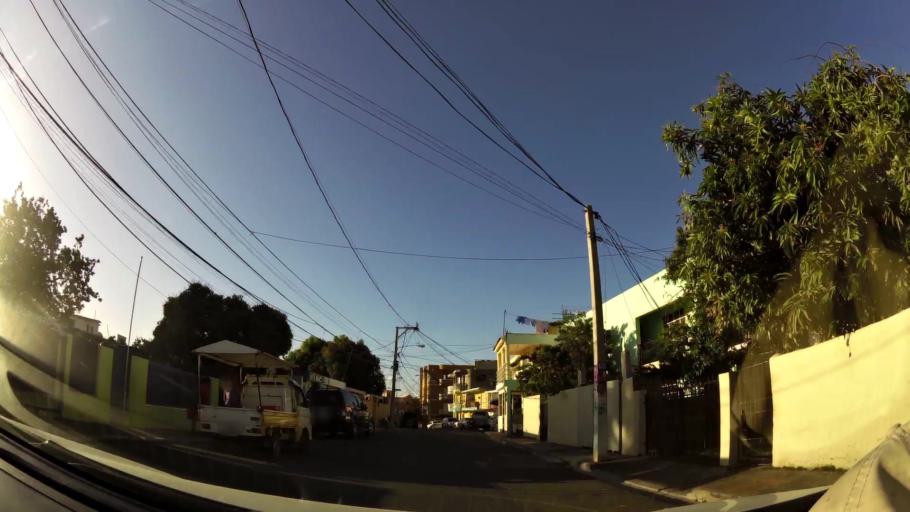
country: DO
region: Nacional
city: Santo Domingo
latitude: 18.4864
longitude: -69.9707
